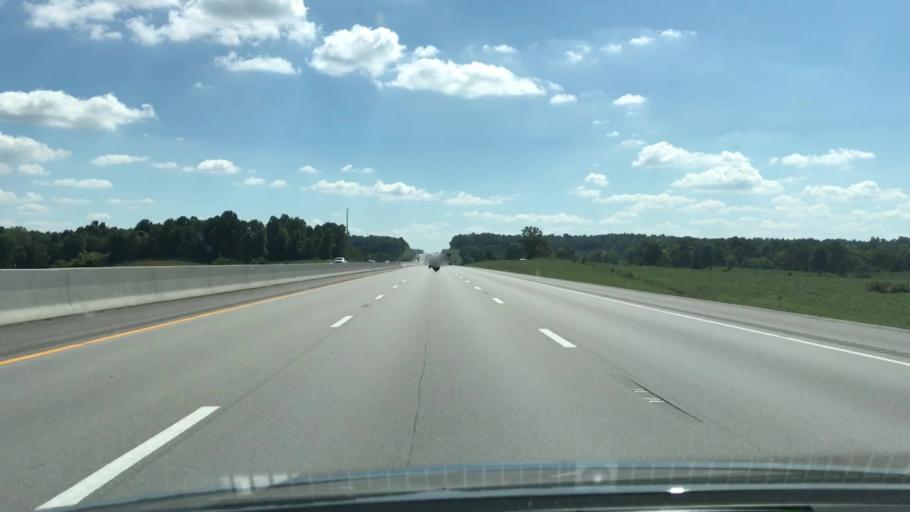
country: US
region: Kentucky
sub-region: Larue County
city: Hodgenville
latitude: 37.4850
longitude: -85.8810
